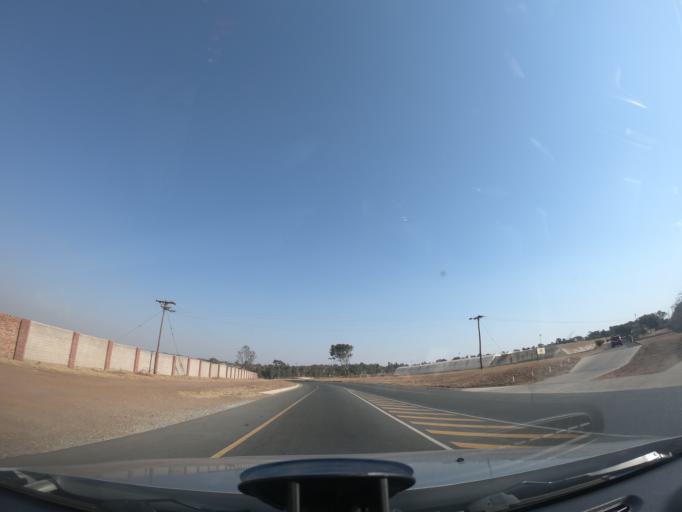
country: ZA
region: Gauteng
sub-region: City of Johannesburg Metropolitan Municipality
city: Diepsloot
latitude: -25.8749
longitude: 28.0283
